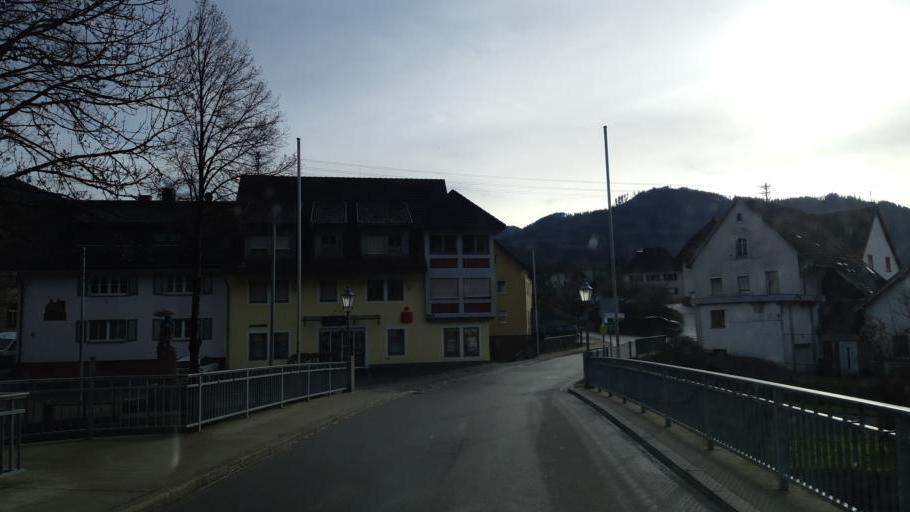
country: DE
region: Baden-Wuerttemberg
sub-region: Freiburg Region
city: Elzach
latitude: 48.1538
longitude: 8.0434
